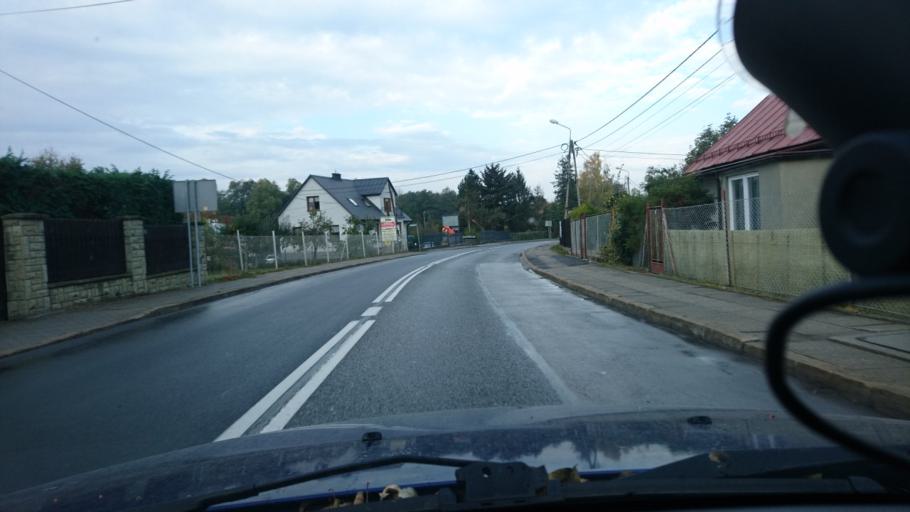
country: PL
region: Silesian Voivodeship
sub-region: Powiat bielski
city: Wilkowice
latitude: 49.7996
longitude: 19.0895
